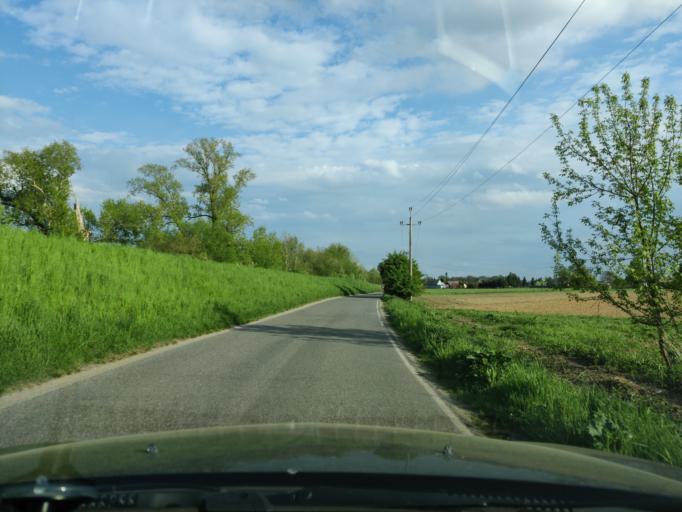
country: PL
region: Masovian Voivodeship
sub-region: Powiat otwocki
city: Jozefow
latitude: 52.1191
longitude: 21.1789
